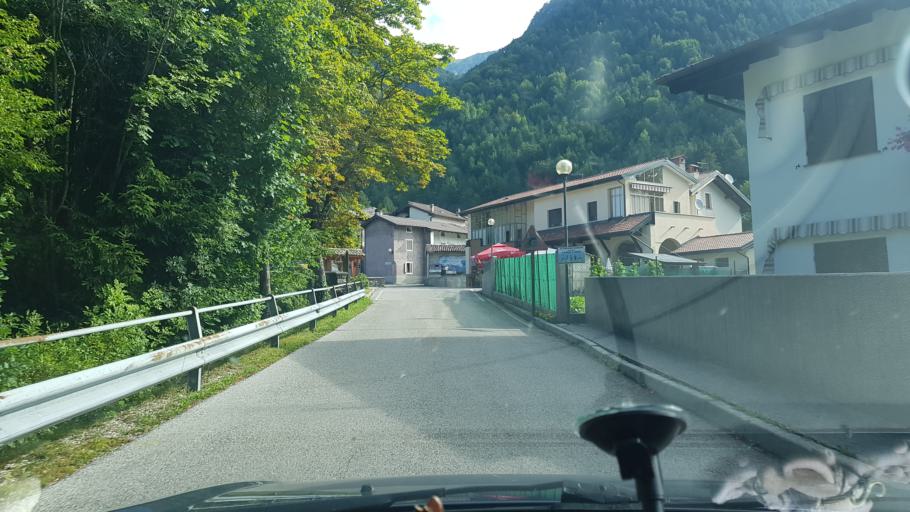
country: IT
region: Friuli Venezia Giulia
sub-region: Provincia di Udine
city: Prato
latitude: 46.3624
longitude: 13.3505
